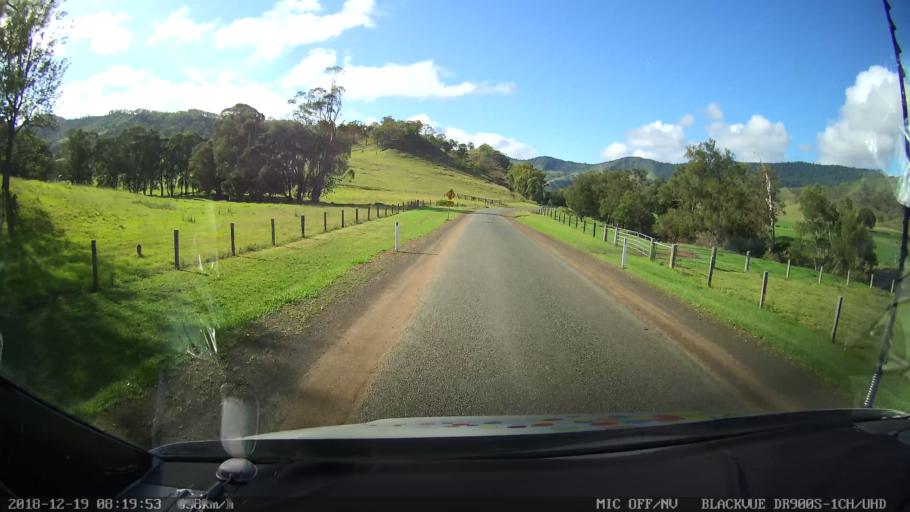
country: AU
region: New South Wales
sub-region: Kyogle
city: Kyogle
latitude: -28.2859
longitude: 152.9098
